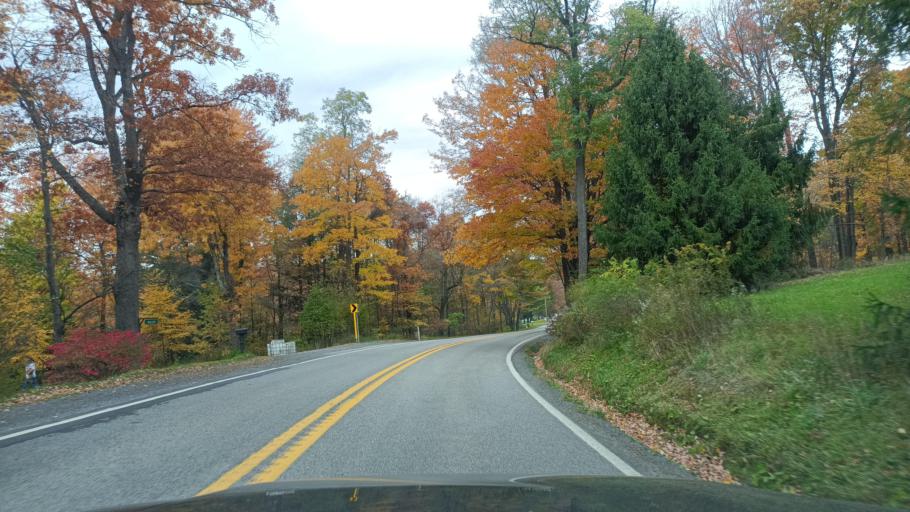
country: US
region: Maryland
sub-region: Garrett County
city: Mountain Lake Park
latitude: 39.2257
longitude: -79.2158
